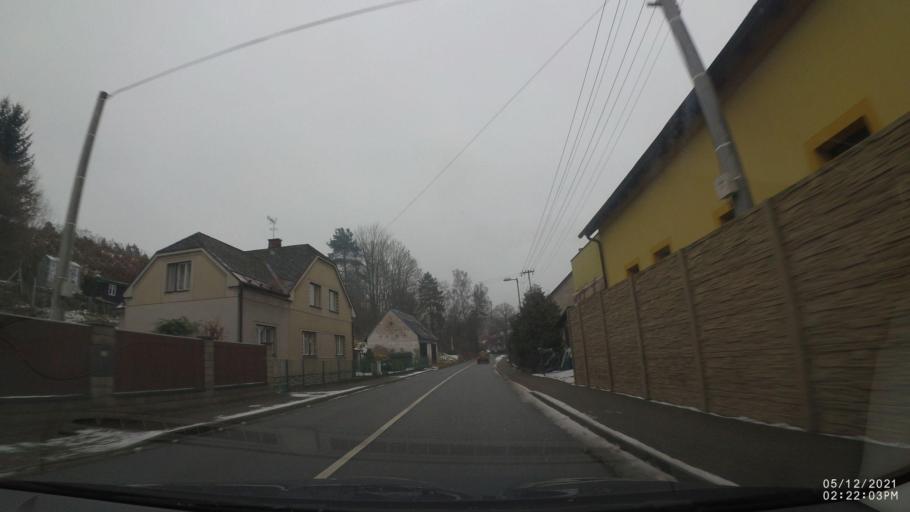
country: CZ
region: Kralovehradecky
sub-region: Okres Nachod
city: Nachod
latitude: 50.4347
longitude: 16.1572
